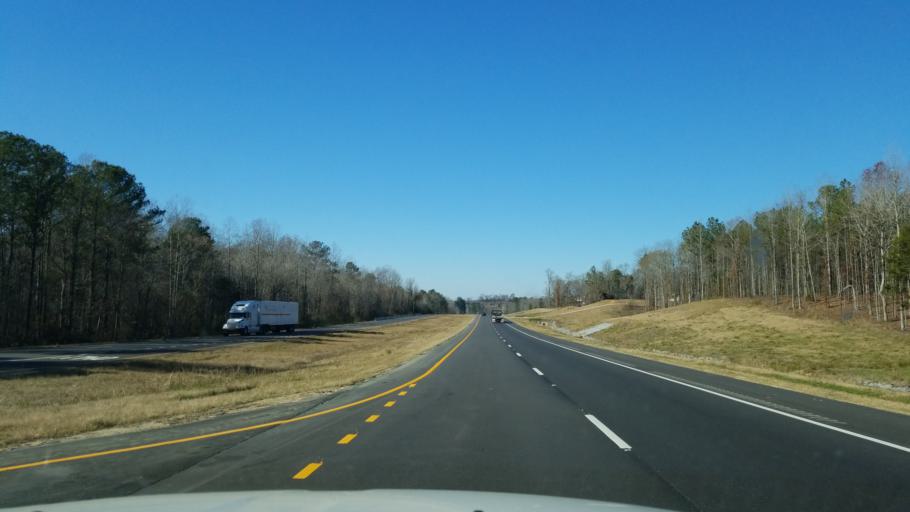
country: US
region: Alabama
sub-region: Pickens County
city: Reform
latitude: 33.3627
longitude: -87.9765
